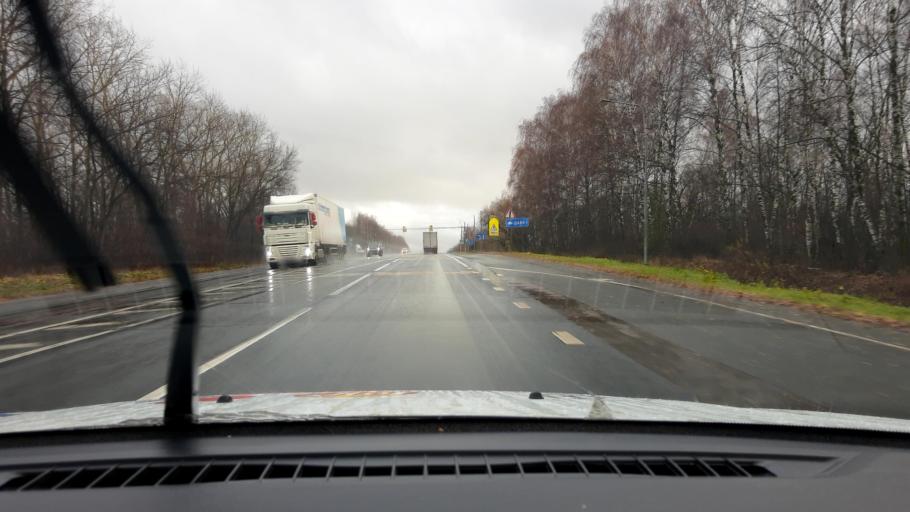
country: RU
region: Nizjnij Novgorod
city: Pamyat' Parizhskoy Kommuny
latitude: 56.0574
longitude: 44.3959
